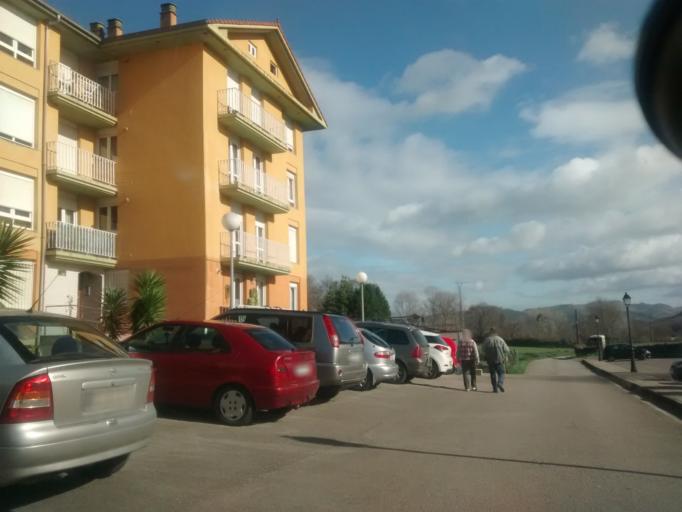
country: ES
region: Cantabria
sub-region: Provincia de Cantabria
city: Lierganes
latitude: 43.3453
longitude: -3.7406
